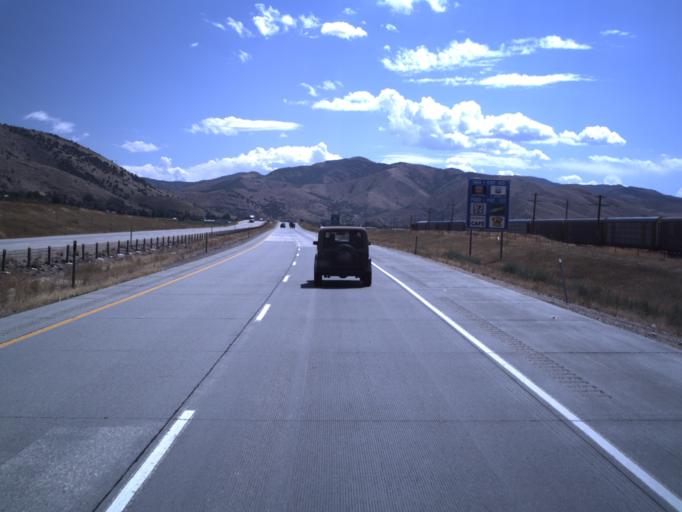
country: US
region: Utah
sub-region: Morgan County
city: Morgan
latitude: 41.0584
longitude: -111.6995
